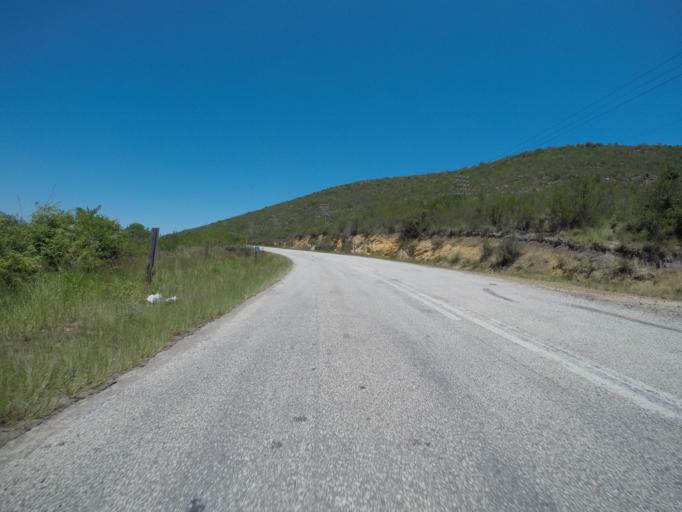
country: ZA
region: Eastern Cape
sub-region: Cacadu District Municipality
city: Kareedouw
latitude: -33.8788
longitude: 24.0535
